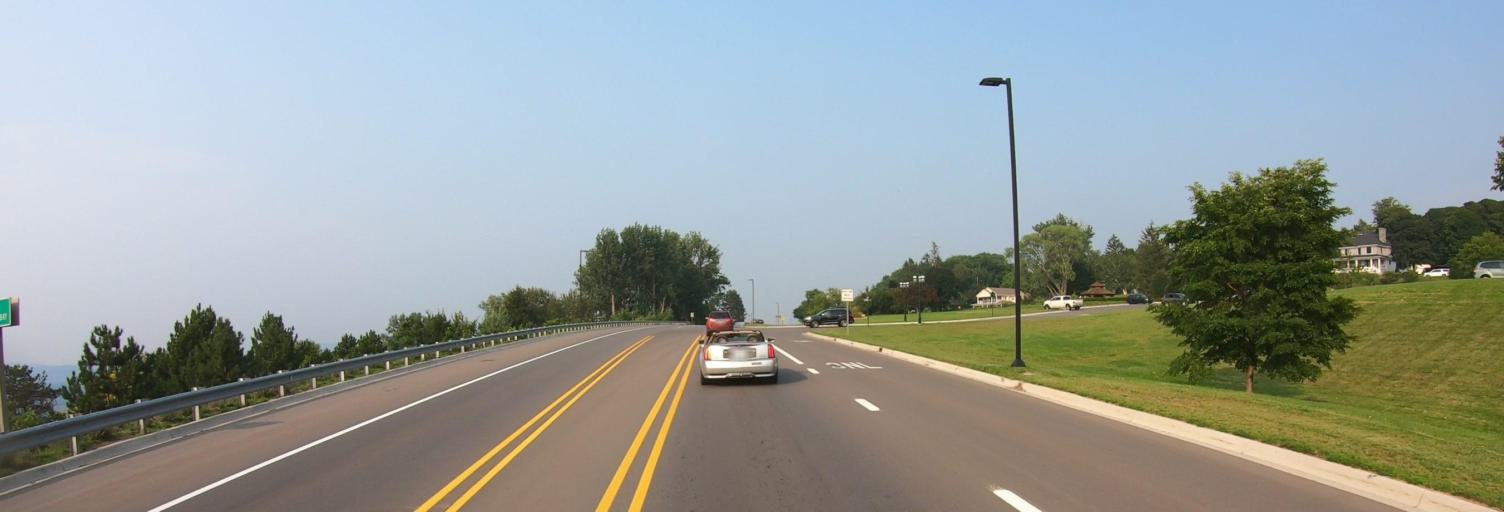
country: US
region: Michigan
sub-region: Emmet County
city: Petoskey
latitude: 45.3777
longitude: -84.9567
